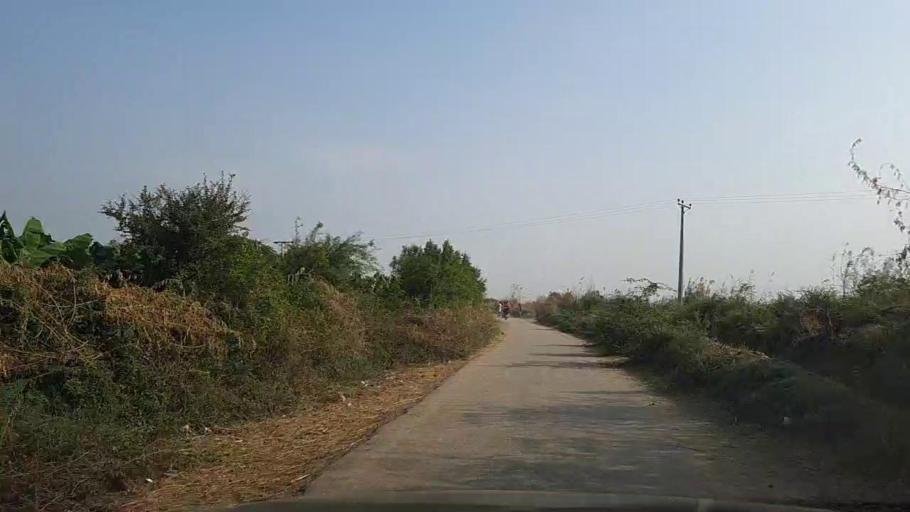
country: PK
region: Sindh
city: Thatta
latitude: 24.6503
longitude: 67.9243
